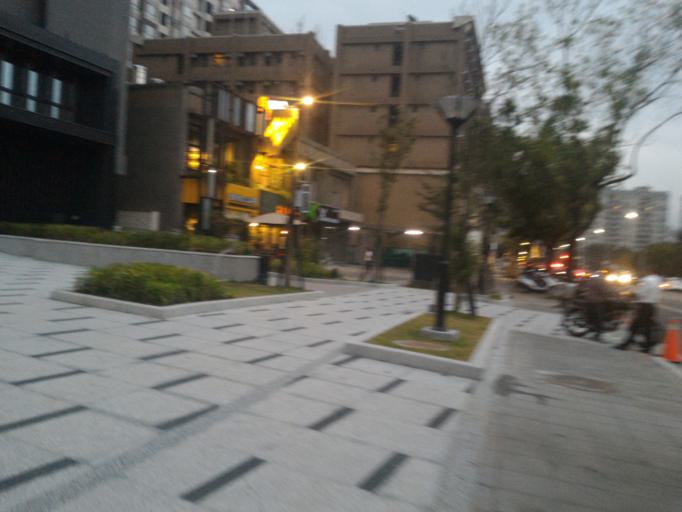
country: TW
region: Taiwan
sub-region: Taoyuan
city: Taoyuan
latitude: 24.9471
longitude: 121.3722
